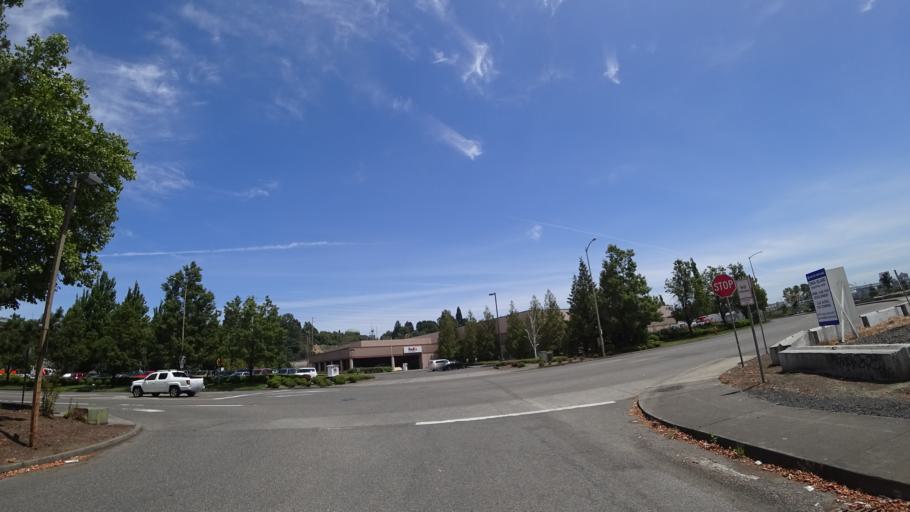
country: US
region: Oregon
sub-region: Multnomah County
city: Portland
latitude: 45.5552
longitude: -122.6987
